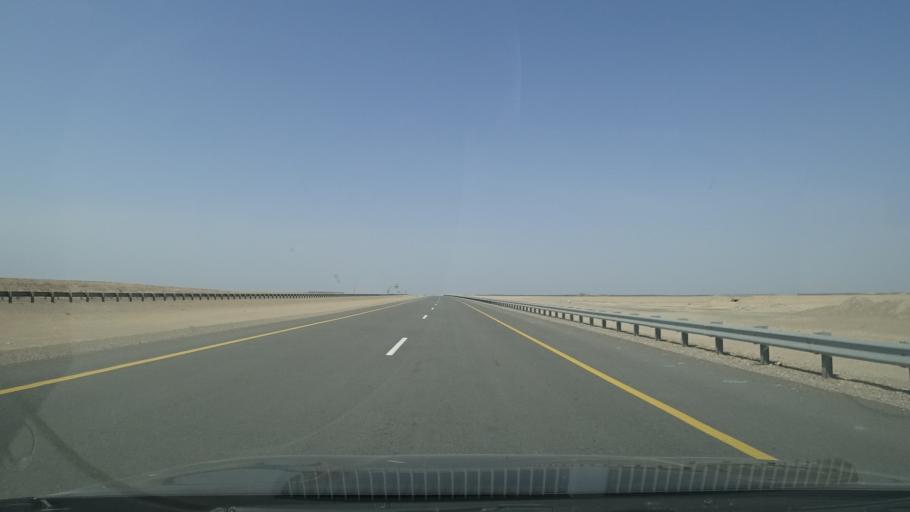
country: OM
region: Muhafazat ad Dakhiliyah
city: Adam
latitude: 22.0182
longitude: 57.4923
